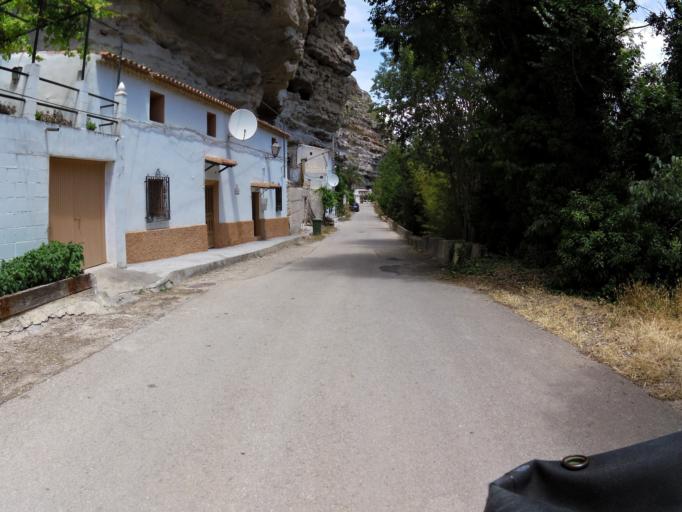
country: ES
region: Castille-La Mancha
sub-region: Provincia de Albacete
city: Jorquera
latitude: 39.1577
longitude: -1.5718
